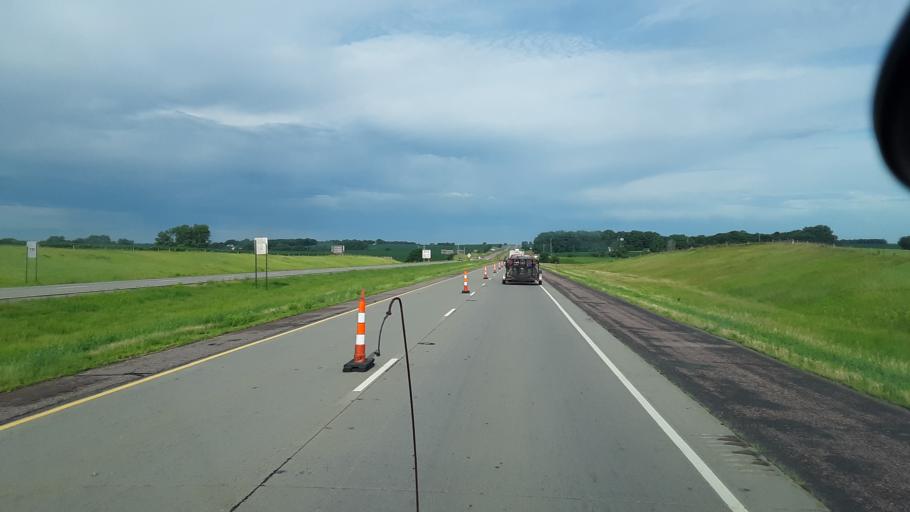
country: US
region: South Dakota
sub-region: Minnehaha County
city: Crooks
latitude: 43.6088
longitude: -96.8203
